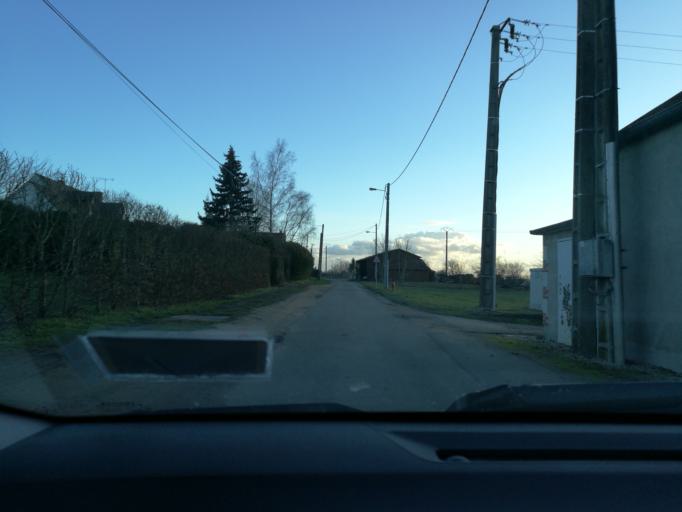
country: FR
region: Centre
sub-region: Departement du Loiret
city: Saint-Jean-de-Braye
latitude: 47.9302
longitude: 1.9689
